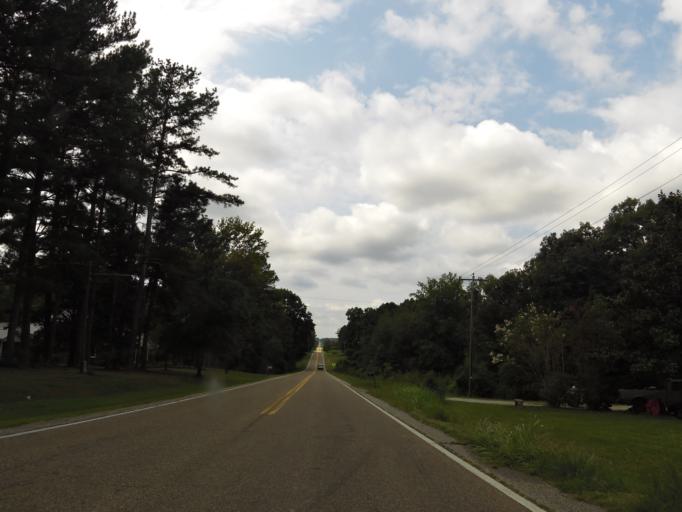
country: US
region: Tennessee
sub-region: Decatur County
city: Decaturville
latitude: 35.5199
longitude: -88.2738
